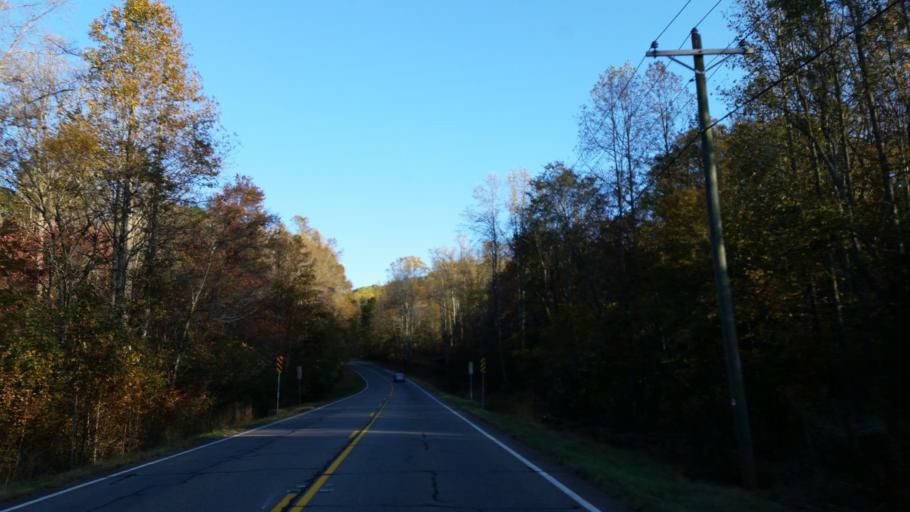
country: US
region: Georgia
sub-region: Pickens County
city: Jasper
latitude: 34.5926
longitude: -84.3218
